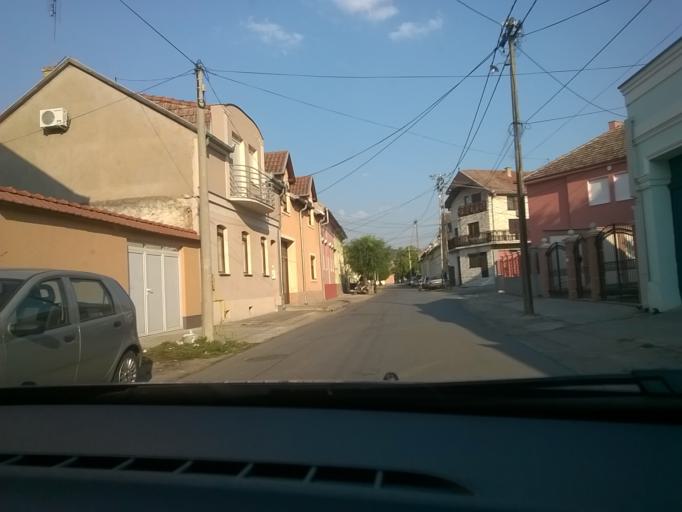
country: RS
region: Autonomna Pokrajina Vojvodina
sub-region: Juznobanatski Okrug
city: Vrsac
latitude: 45.1164
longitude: 21.2924
